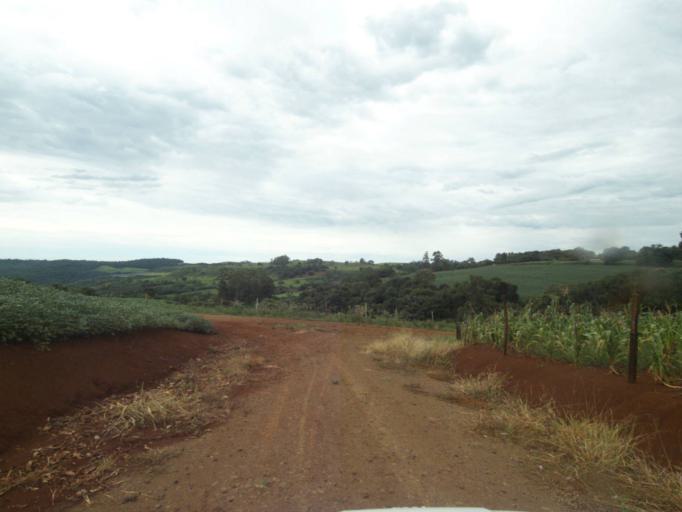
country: BR
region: Parana
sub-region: Guaraniacu
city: Guaraniacu
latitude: -24.9197
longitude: -52.9412
